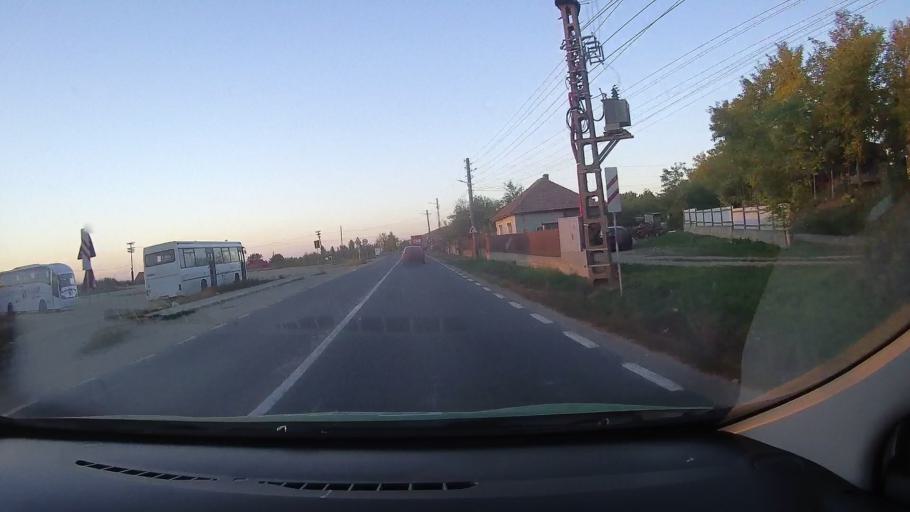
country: RO
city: Szekelyhid
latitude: 47.3590
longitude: 22.1116
